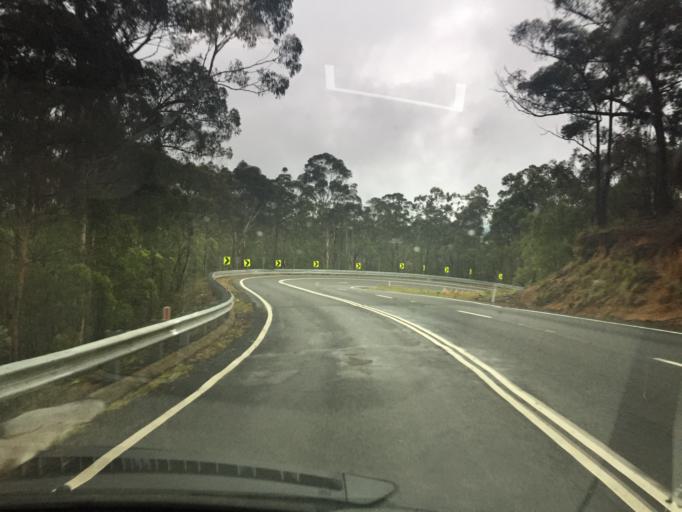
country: AU
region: New South Wales
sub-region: Bega Valley
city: Bega
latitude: -36.6108
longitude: 149.4748
